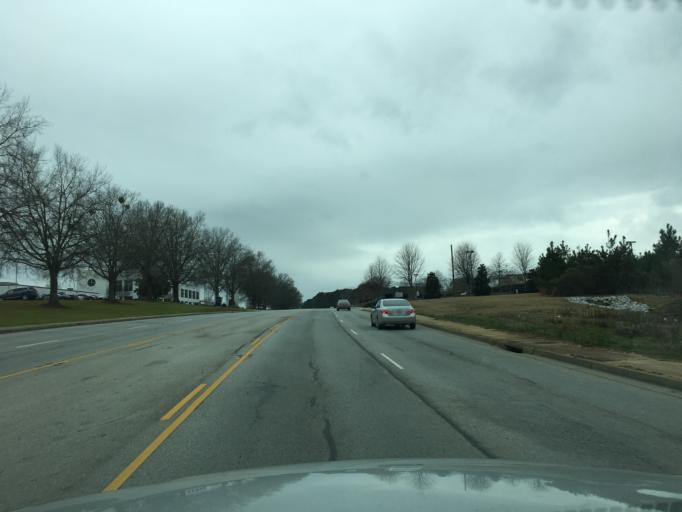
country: US
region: South Carolina
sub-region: Greenwood County
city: Greenwood
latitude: 34.2090
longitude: -82.1185
